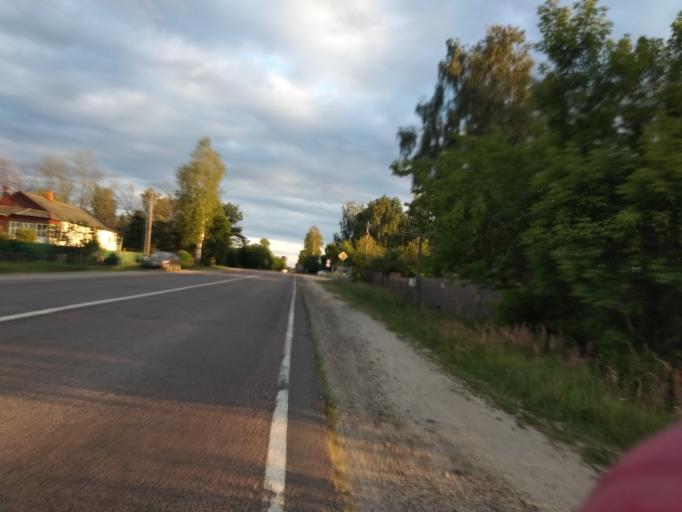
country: RU
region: Moskovskaya
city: Misheronskiy
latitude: 55.6003
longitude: 39.7056
